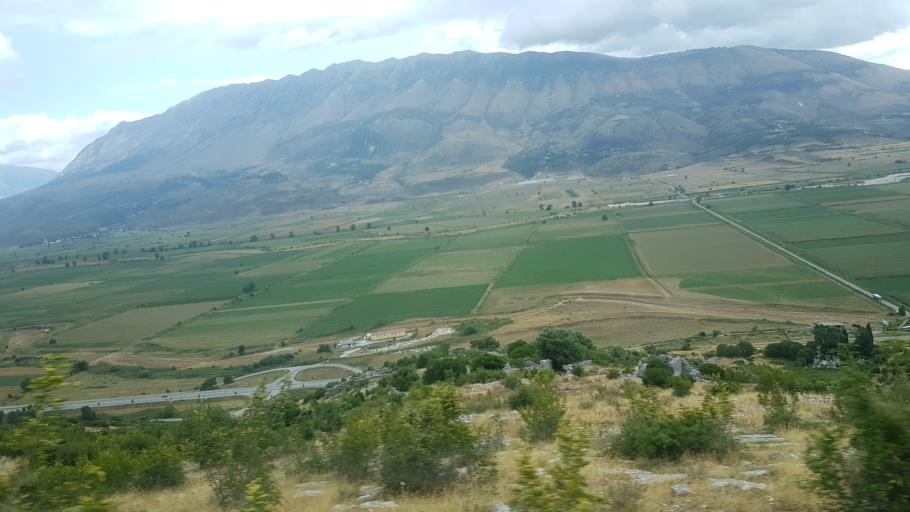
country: AL
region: Gjirokaster
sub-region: Rrethi i Gjirokastres
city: Libohove
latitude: 39.9475
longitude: 20.2509
